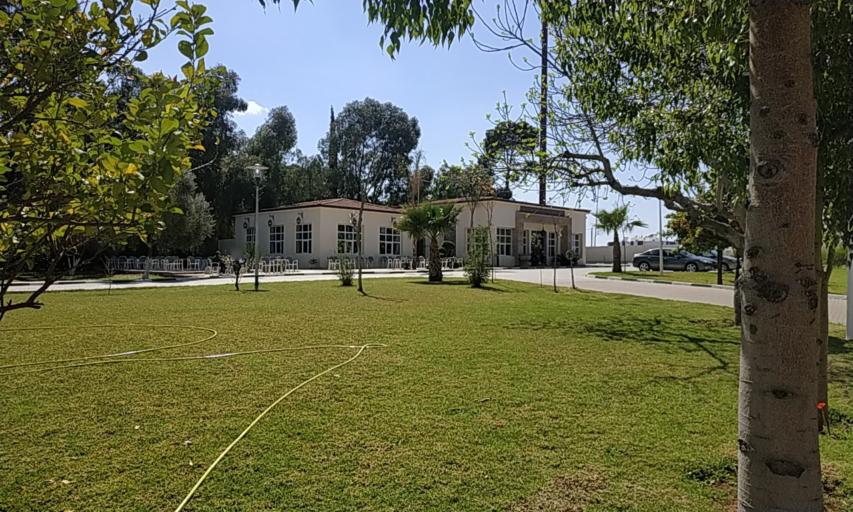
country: MA
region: Fes-Boulemane
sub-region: Fes
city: Oulad Tayeb
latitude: 33.9875
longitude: -5.0203
